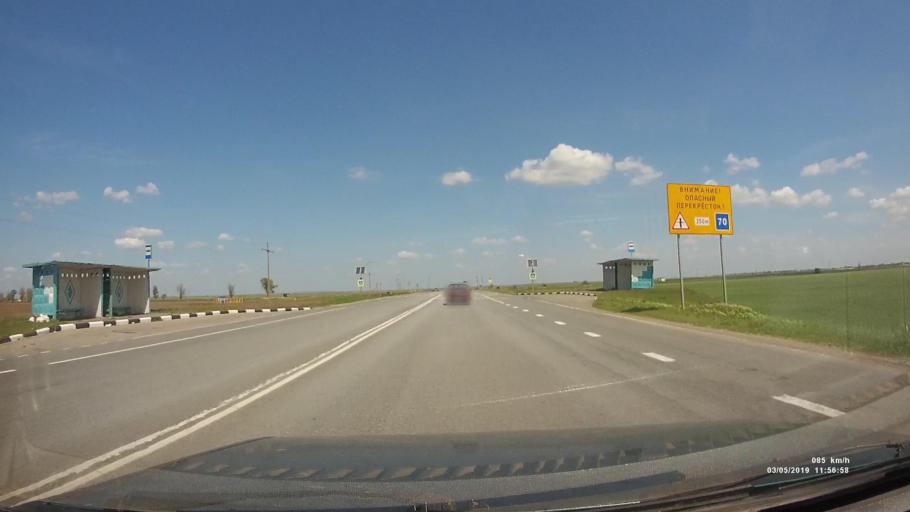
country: RU
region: Rostov
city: Bagayevskaya
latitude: 47.2010
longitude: 40.3065
